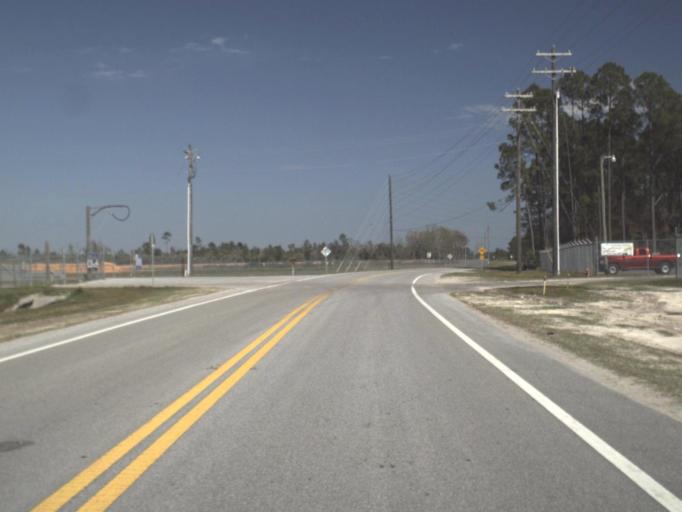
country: US
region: Florida
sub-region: Bay County
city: Lynn Haven
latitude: 30.3223
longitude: -85.6580
